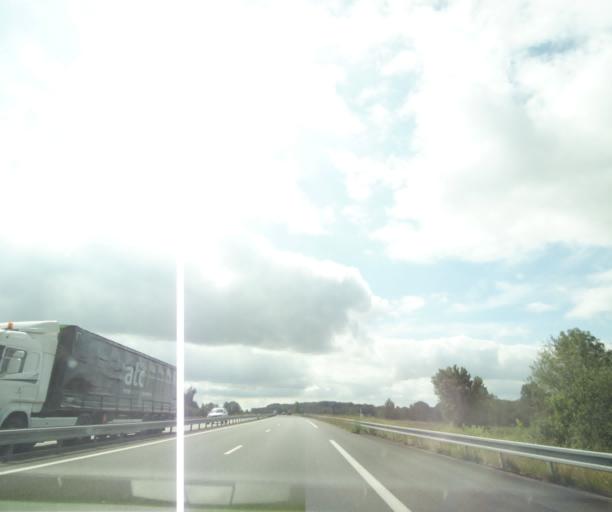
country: FR
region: Pays de la Loire
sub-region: Departement de Maine-et-Loire
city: Vivy
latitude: 47.3444
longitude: -0.0676
